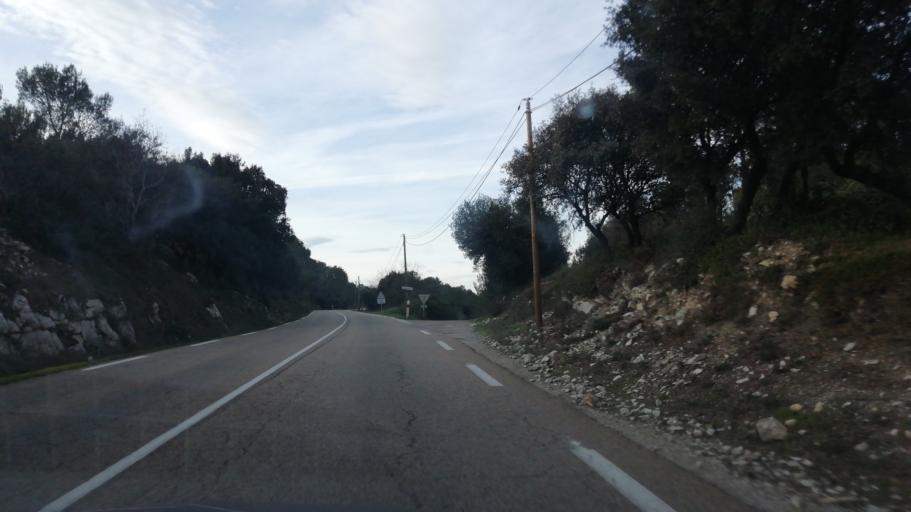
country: FR
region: Languedoc-Roussillon
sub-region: Departement du Gard
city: Caveirac
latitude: 43.8465
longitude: 4.2951
